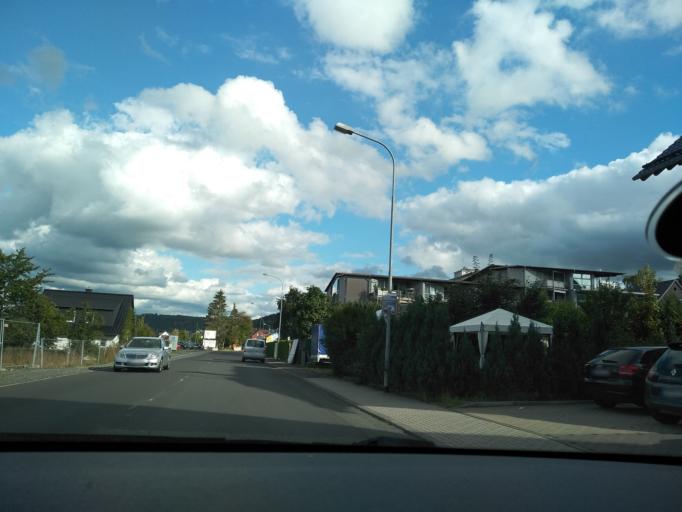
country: DE
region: Hesse
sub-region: Regierungsbezirk Giessen
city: Haiger
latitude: 50.7439
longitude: 8.1988
